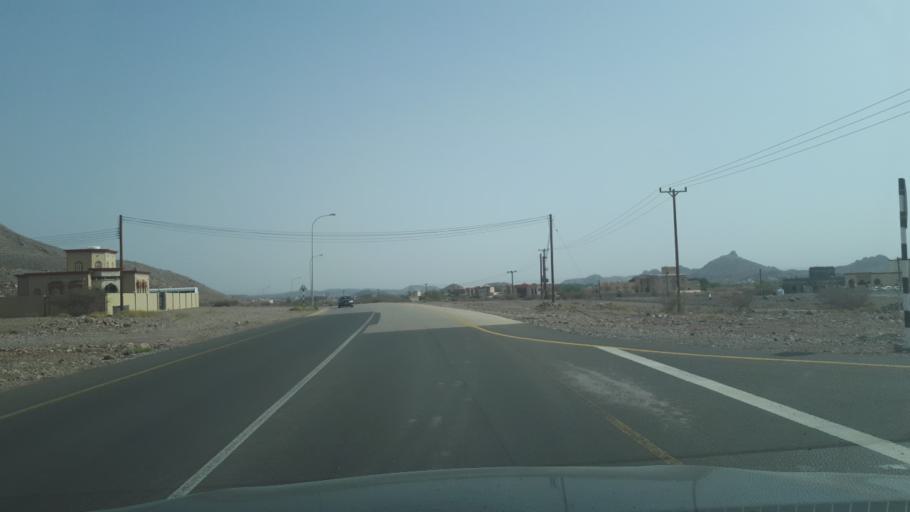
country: OM
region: Az Zahirah
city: `Ibri
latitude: 23.1843
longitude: 56.9211
